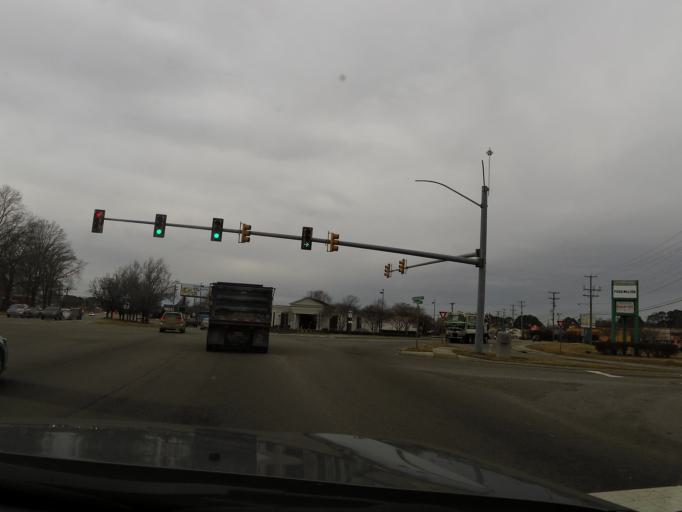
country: US
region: Virginia
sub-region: City of Portsmouth
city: Portsmouth Heights
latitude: 36.8604
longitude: -76.3912
